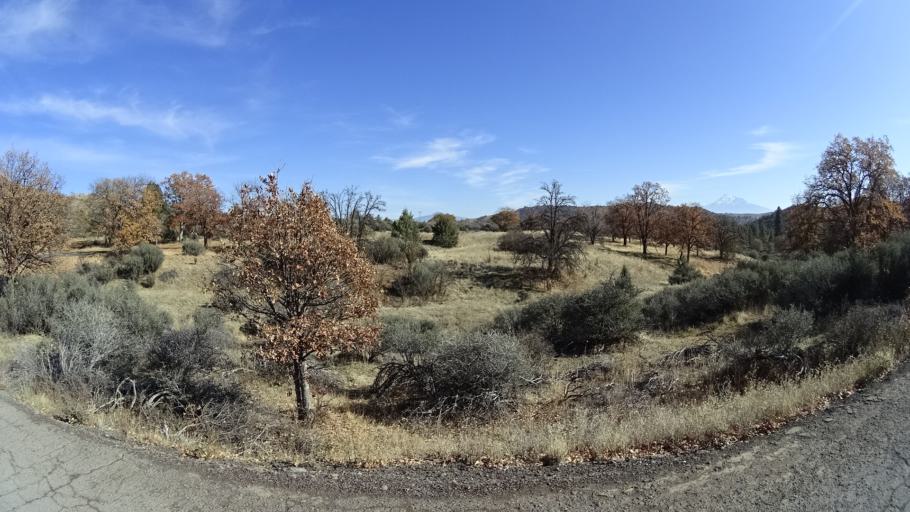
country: US
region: California
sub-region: Siskiyou County
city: Yreka
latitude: 41.7698
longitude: -122.6377
